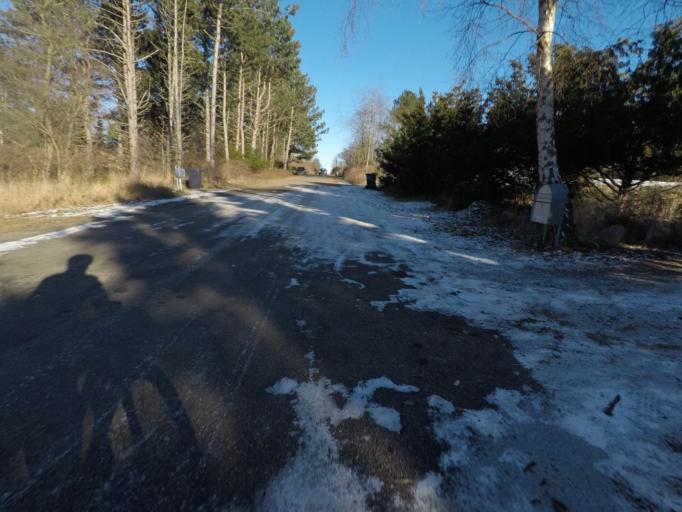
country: DK
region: Capital Region
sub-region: Halsnaes Kommune
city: Liseleje
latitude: 55.9998
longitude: 11.9345
